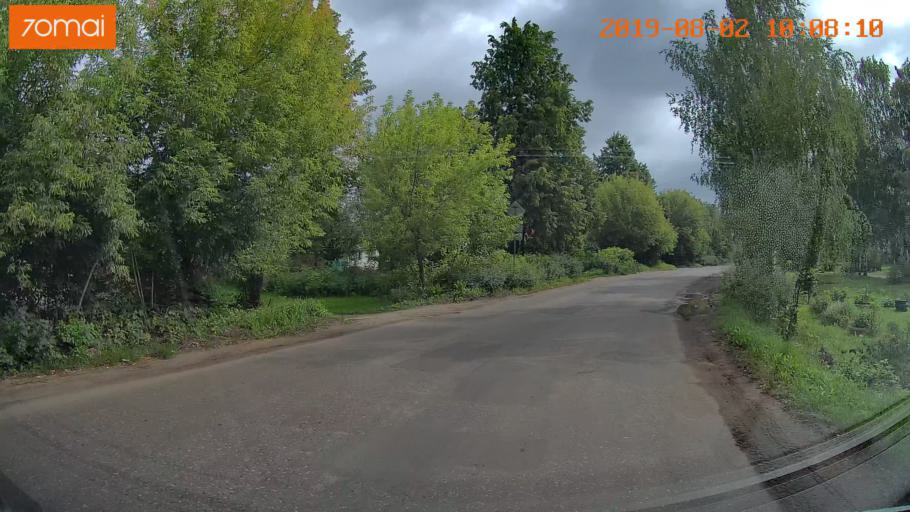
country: RU
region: Ivanovo
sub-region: Gorod Ivanovo
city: Ivanovo
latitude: 56.9855
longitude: 40.9374
